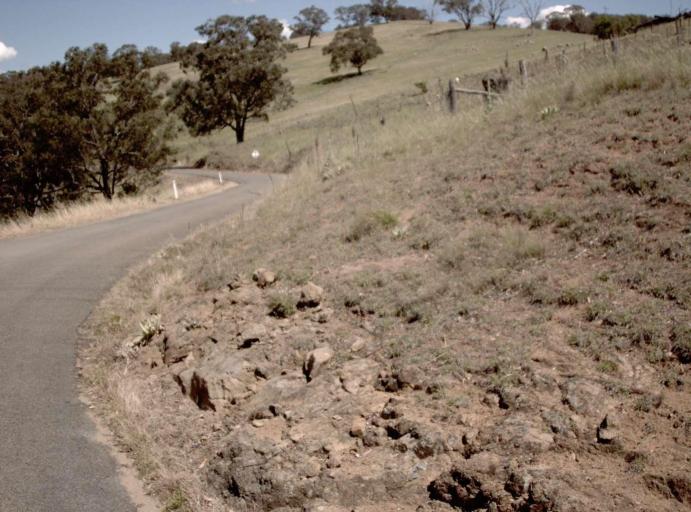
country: AU
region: New South Wales
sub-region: Snowy River
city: Jindabyne
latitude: -37.0663
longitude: 148.5836
